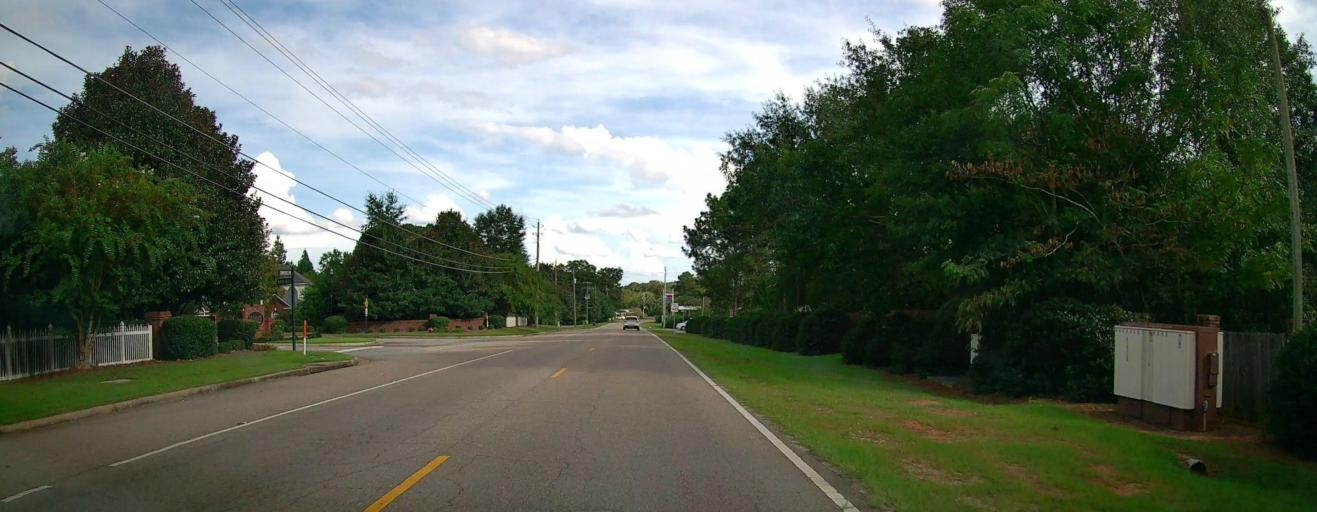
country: US
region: Alabama
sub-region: Russell County
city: Phenix City
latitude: 32.5136
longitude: -85.0229
